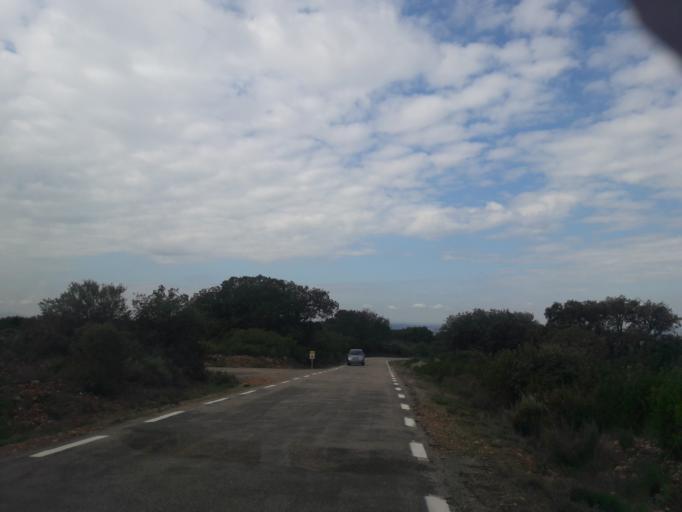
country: ES
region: Castille and Leon
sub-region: Provincia de Salamanca
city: Serradilla del Arroyo
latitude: 40.5407
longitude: -6.3904
